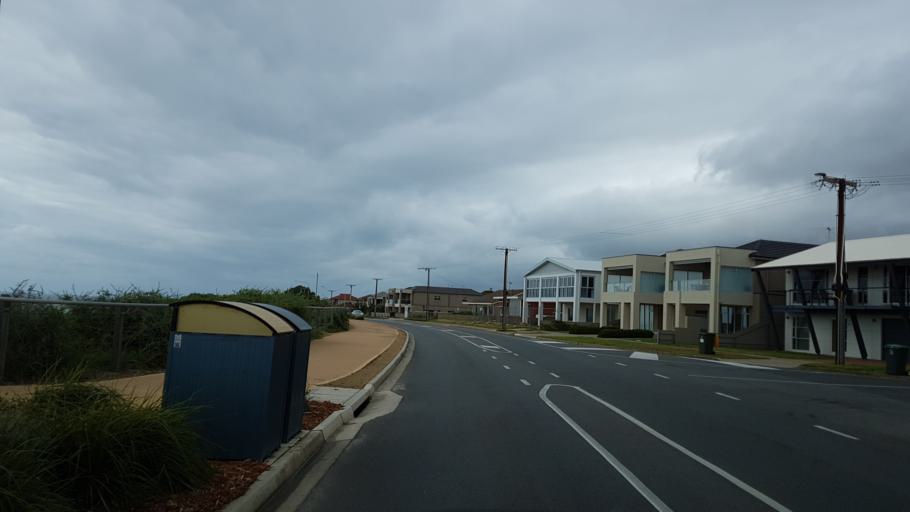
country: AU
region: South Australia
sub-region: Onkaparinga
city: Port Willunga
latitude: -35.2814
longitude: 138.4439
